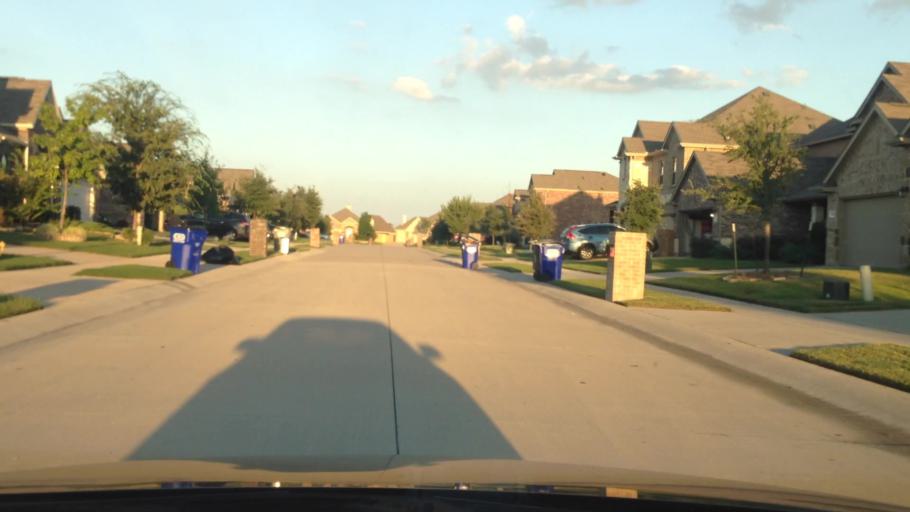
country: US
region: Texas
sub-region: Denton County
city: Little Elm
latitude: 33.1382
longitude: -96.9297
